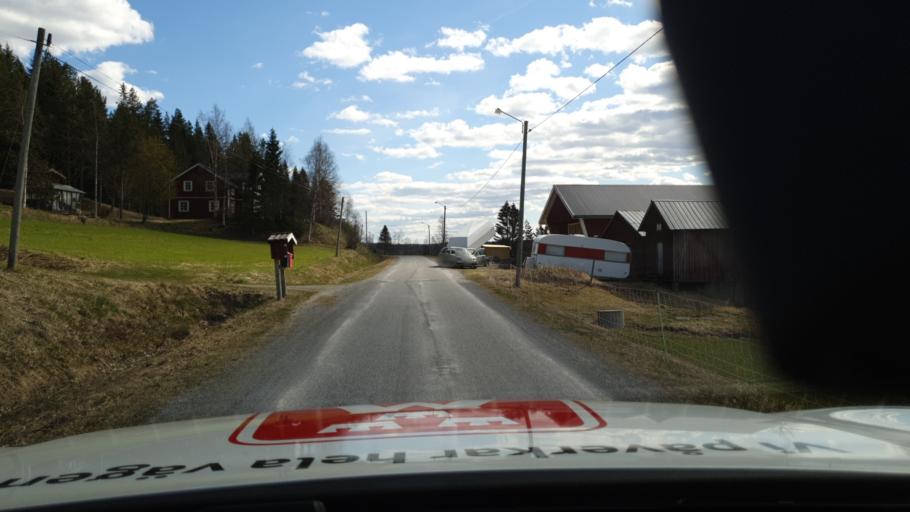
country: SE
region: Jaemtland
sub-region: Bergs Kommun
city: Hoverberg
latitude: 62.8396
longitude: 14.4110
